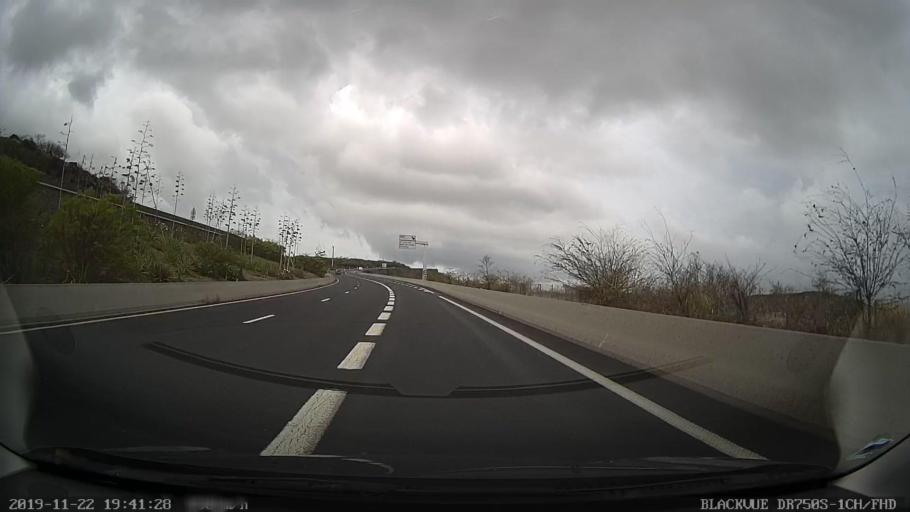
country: RE
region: Reunion
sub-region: Reunion
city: Saint-Paul
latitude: -21.0365
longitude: 55.2481
